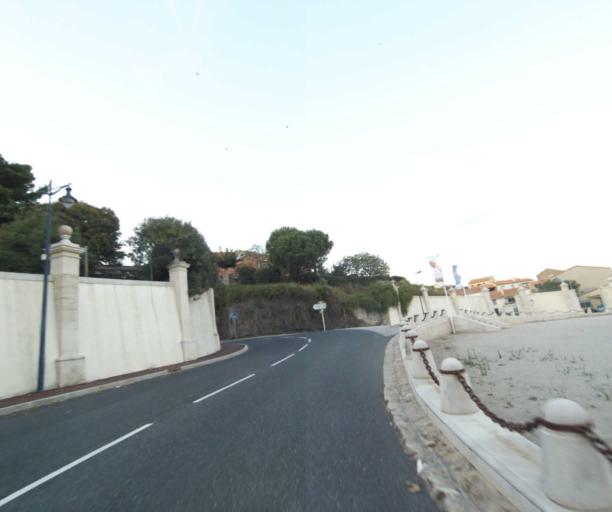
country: FR
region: Languedoc-Roussillon
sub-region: Departement des Pyrenees-Orientales
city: Portvendres
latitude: 42.5210
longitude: 3.1053
